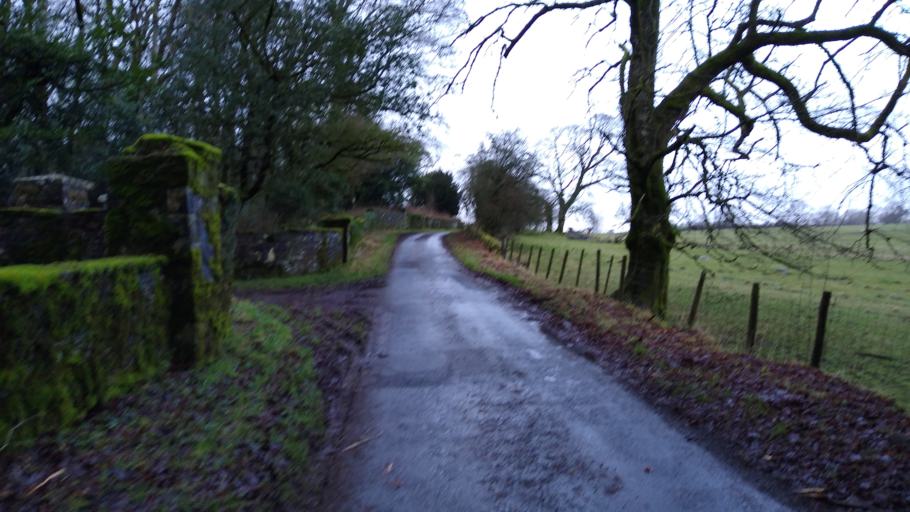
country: GB
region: England
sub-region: Cumbria
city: Wigton
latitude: 54.7220
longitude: -3.1938
